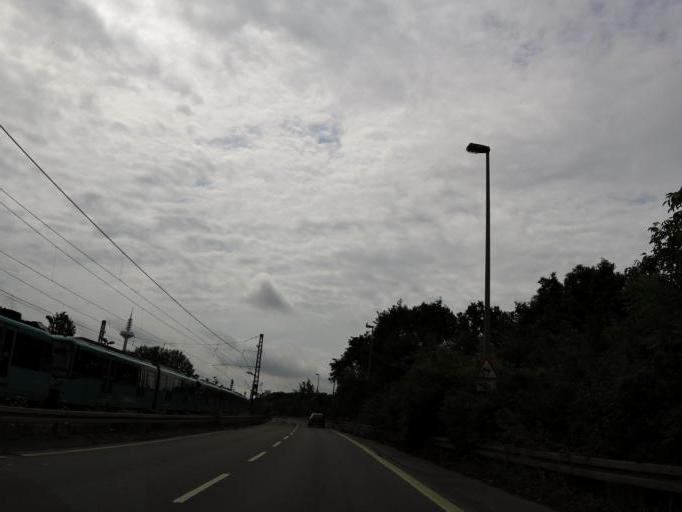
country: DE
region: Hesse
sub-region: Regierungsbezirk Darmstadt
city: Frankfurt am Main
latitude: 50.1502
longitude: 8.6375
